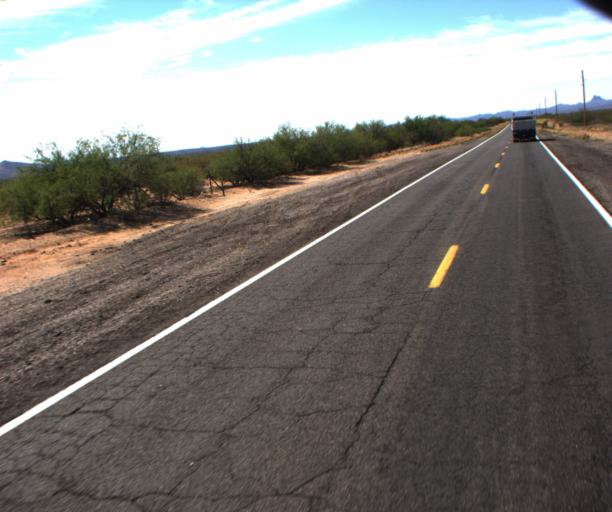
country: US
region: Arizona
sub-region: Yavapai County
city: Congress
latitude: 34.0994
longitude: -112.8299
